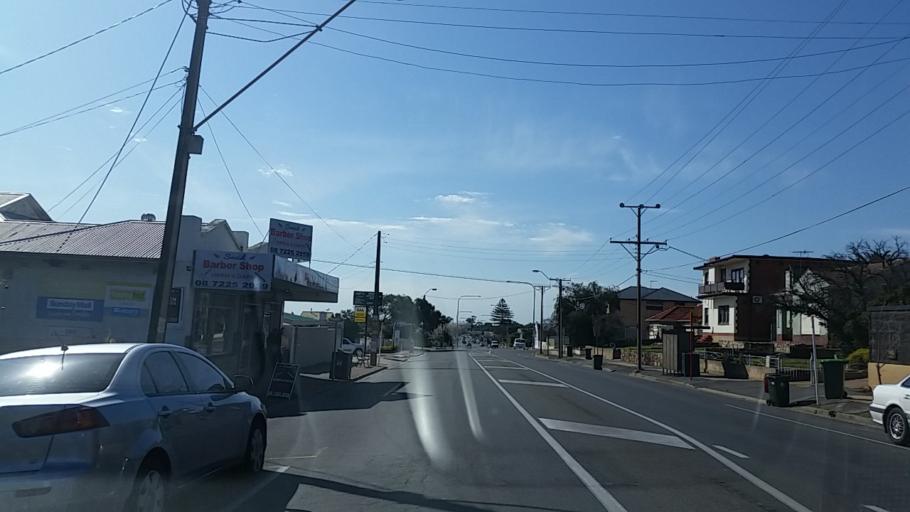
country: AU
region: South Australia
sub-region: Prospect
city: Prospect
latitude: -34.8715
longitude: 138.5929
